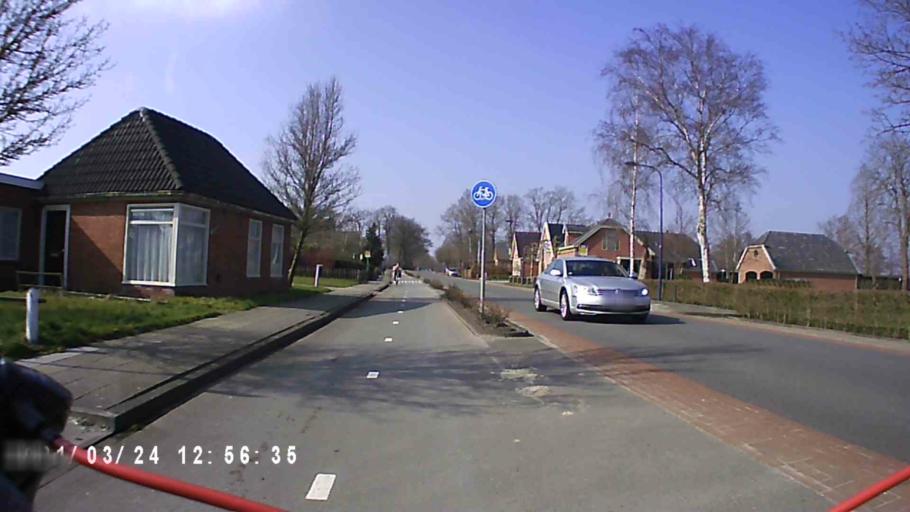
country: NL
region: Groningen
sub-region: Gemeente Grootegast
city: Grootegast
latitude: 53.1521
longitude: 6.3055
